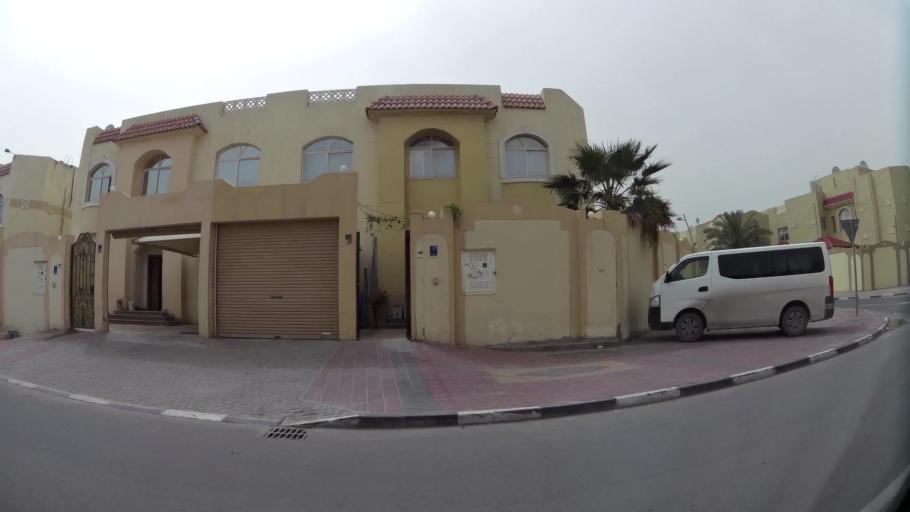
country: QA
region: Baladiyat ad Dawhah
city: Doha
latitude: 25.2374
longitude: 51.5428
